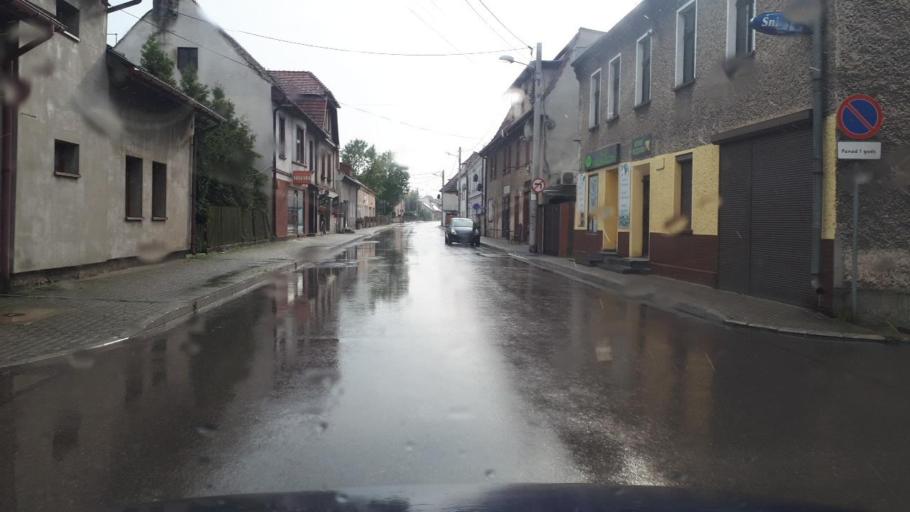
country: PL
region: Silesian Voivodeship
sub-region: Powiat gliwicki
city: Wielowies
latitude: 50.5083
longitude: 18.6144
